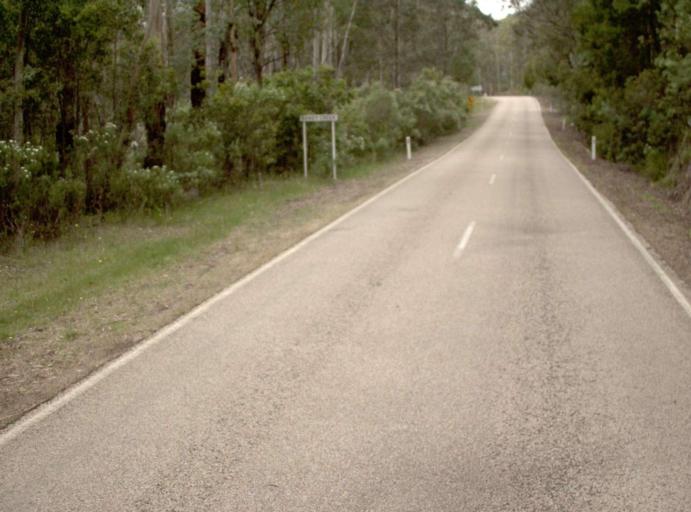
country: AU
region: Victoria
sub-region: East Gippsland
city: Bairnsdale
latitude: -37.6315
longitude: 147.2205
